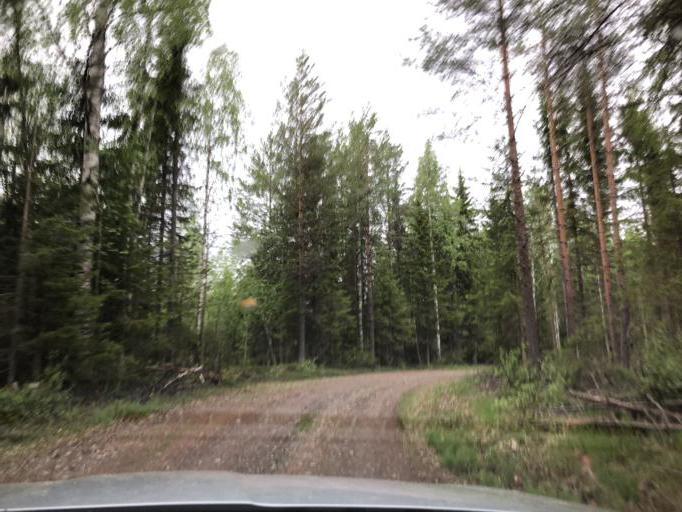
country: SE
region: Norrbotten
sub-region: Pitea Kommun
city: Roknas
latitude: 65.4003
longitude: 21.2630
